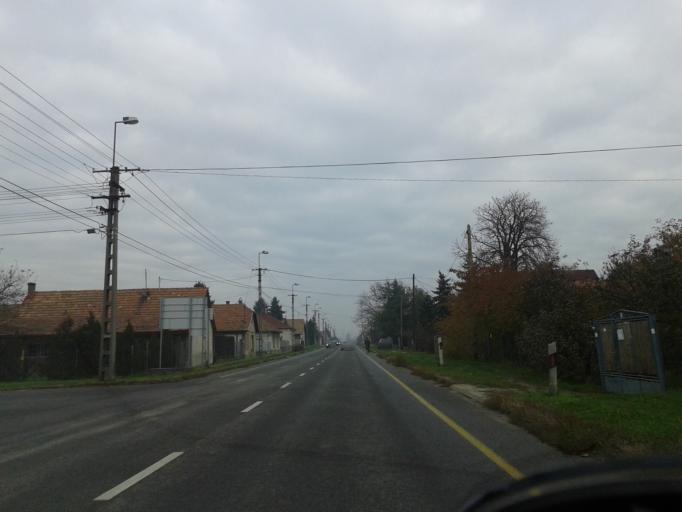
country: HU
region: Fejer
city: Ercsi
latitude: 47.2544
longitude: 18.8927
